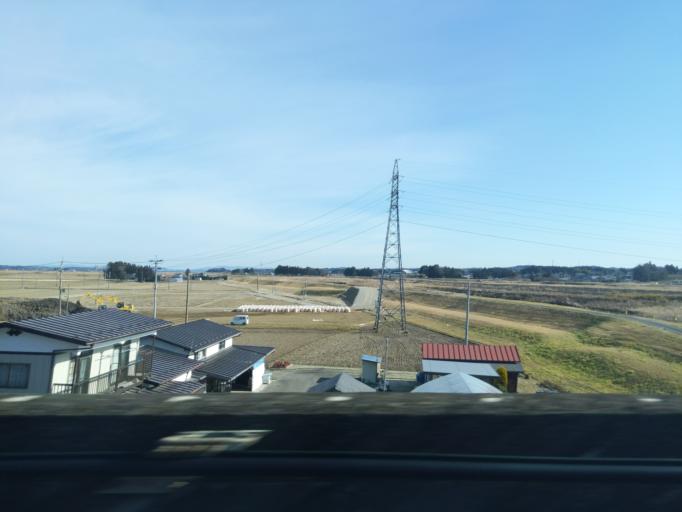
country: JP
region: Miyagi
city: Tomiya
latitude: 38.4271
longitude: 140.9631
